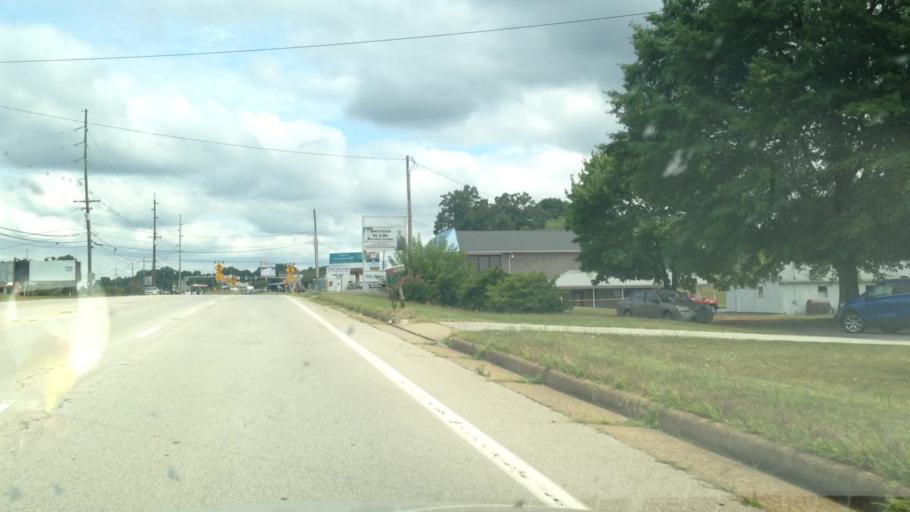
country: US
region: Virginia
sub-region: Pittsylvania County
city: Mount Hermon
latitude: 36.6865
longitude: -79.3691
